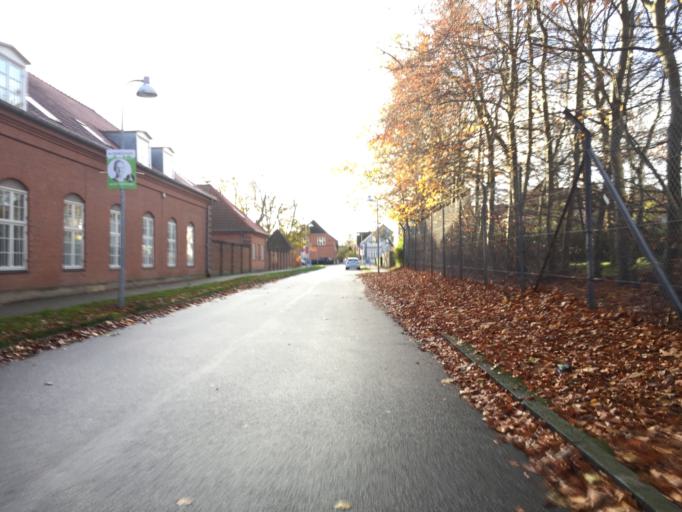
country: DK
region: Zealand
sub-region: Ringsted Kommune
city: Ringsted
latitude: 55.4497
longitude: 11.7940
